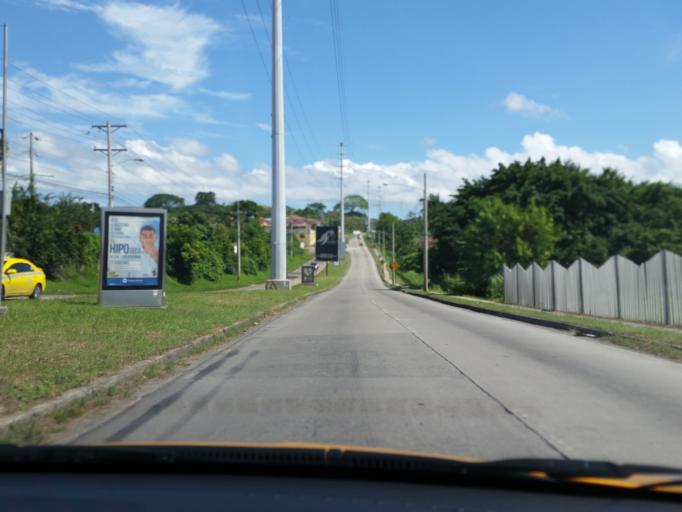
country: PA
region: Panama
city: San Miguelito
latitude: 9.0559
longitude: -79.4616
